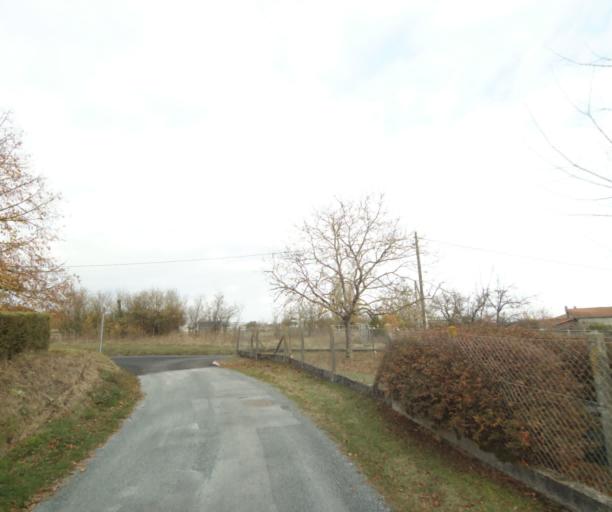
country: FR
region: Poitou-Charentes
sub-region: Departement de la Charente-Maritime
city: Saint-Georges-des-Coteaux
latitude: 45.7693
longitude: -0.7158
